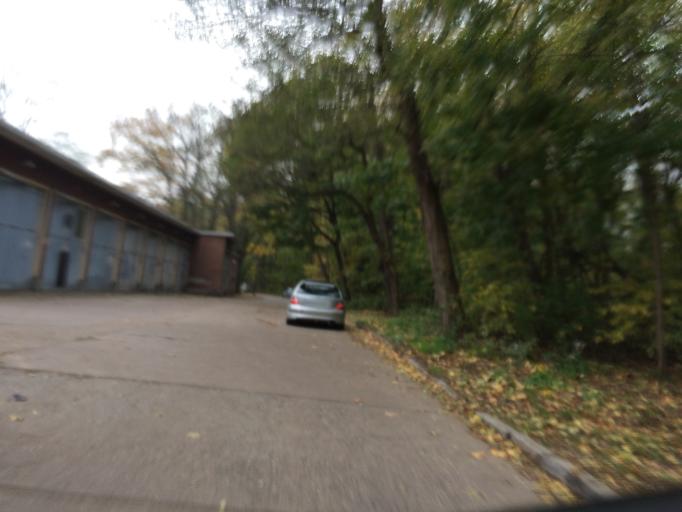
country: DE
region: Berlin
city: Alt-Hohenschoenhausen
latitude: 52.5297
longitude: 13.5078
